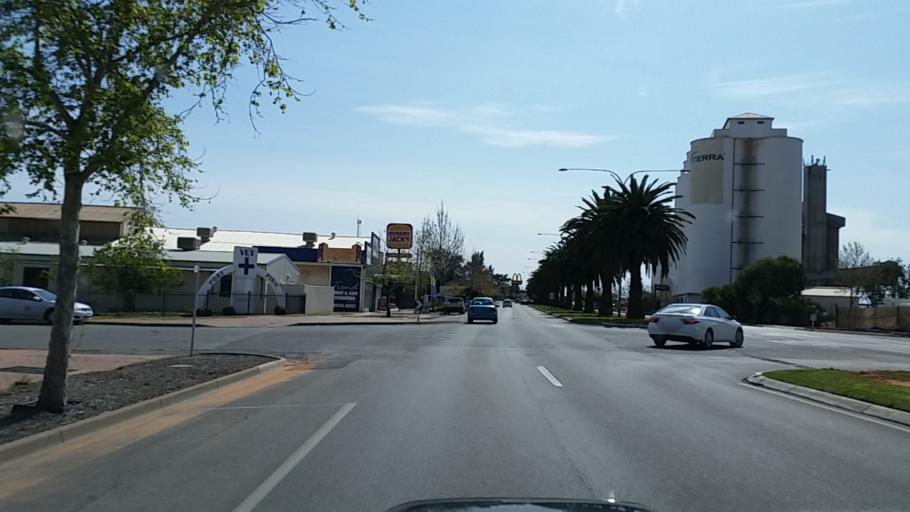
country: AU
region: South Australia
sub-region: Port Pirie City and Dists
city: Port Pirie
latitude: -33.1827
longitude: 138.0160
